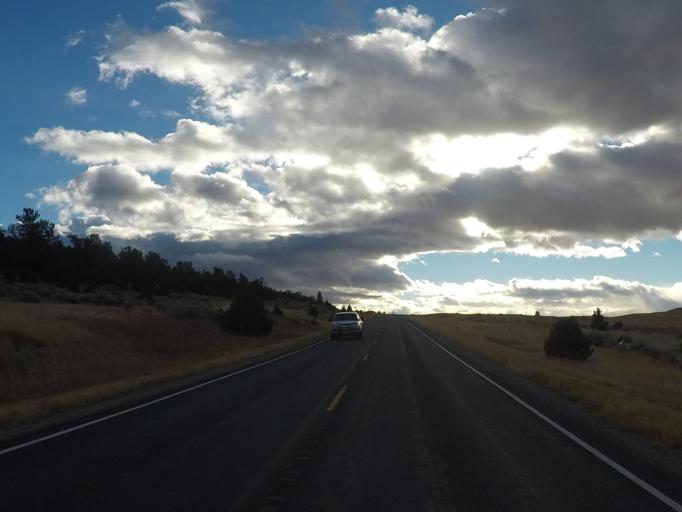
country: US
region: Montana
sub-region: Jefferson County
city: Whitehall
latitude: 45.8965
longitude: -111.9598
